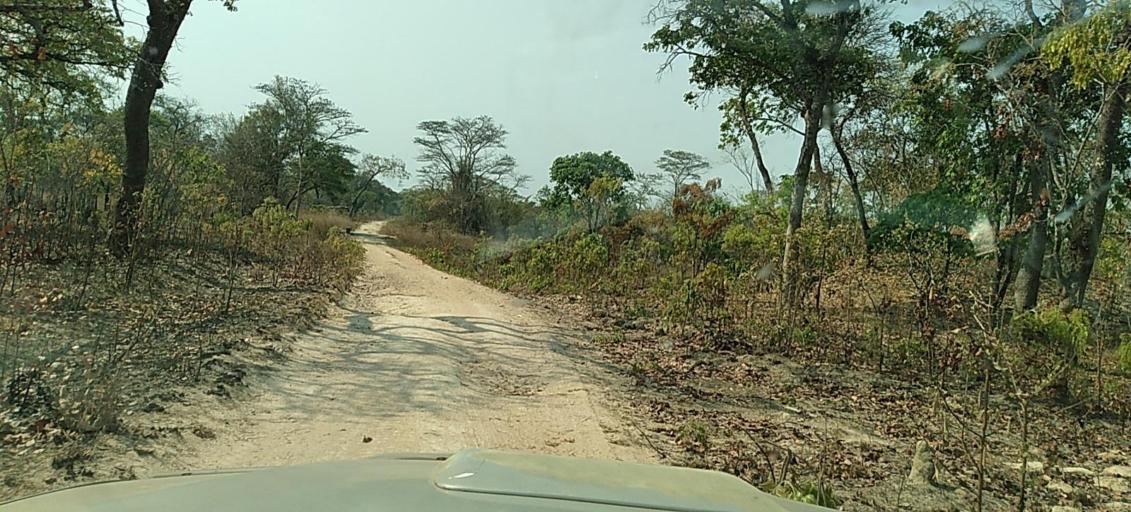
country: ZM
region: North-Western
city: Kasempa
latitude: -13.5413
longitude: 26.4088
